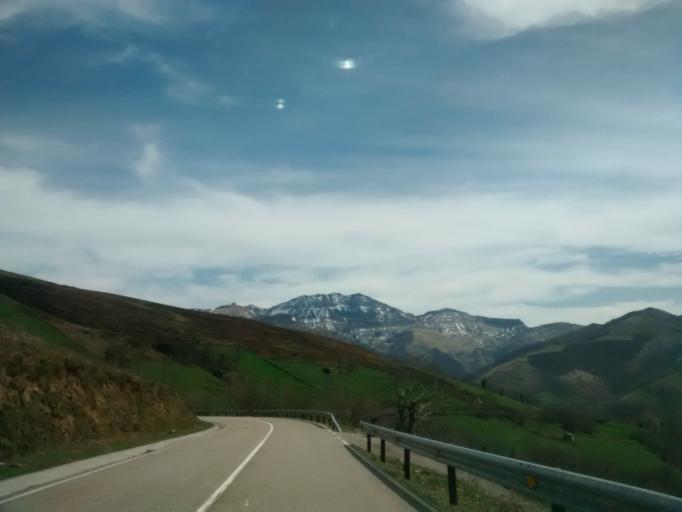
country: ES
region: Cantabria
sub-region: Provincia de Cantabria
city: Vega de Pas
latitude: 43.1705
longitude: -3.7846
